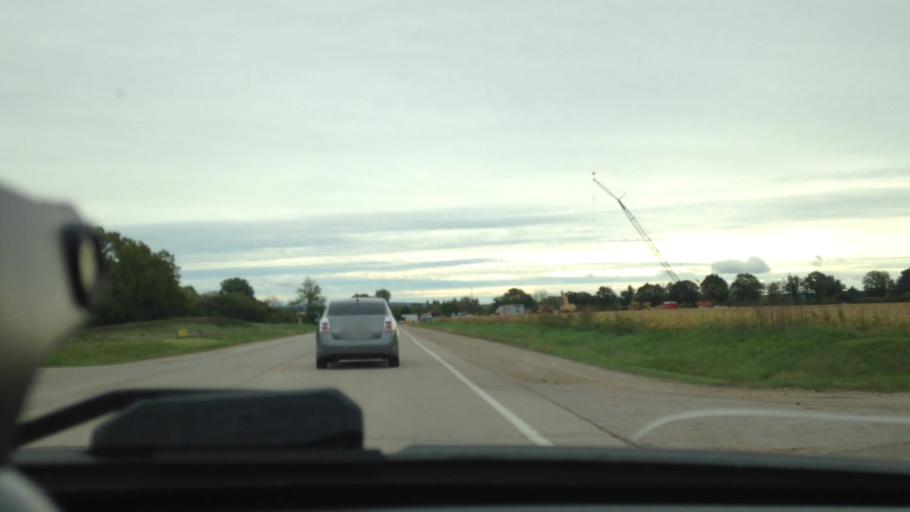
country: US
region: Wisconsin
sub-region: Fond du Lac County
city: North Fond du Lac
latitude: 43.7993
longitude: -88.4928
